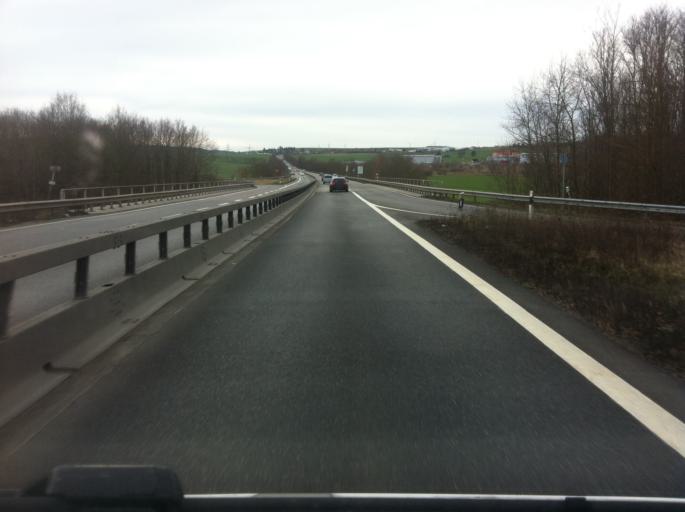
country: DE
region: Rheinland-Pfalz
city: Kottenheim
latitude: 50.3486
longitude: 7.2663
